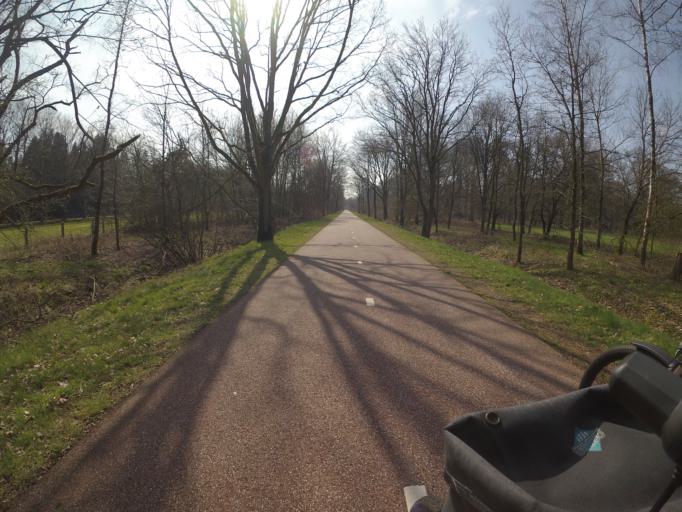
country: NL
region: North Brabant
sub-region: Gemeente Goirle
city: Goirle
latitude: 51.5599
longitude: 5.0226
